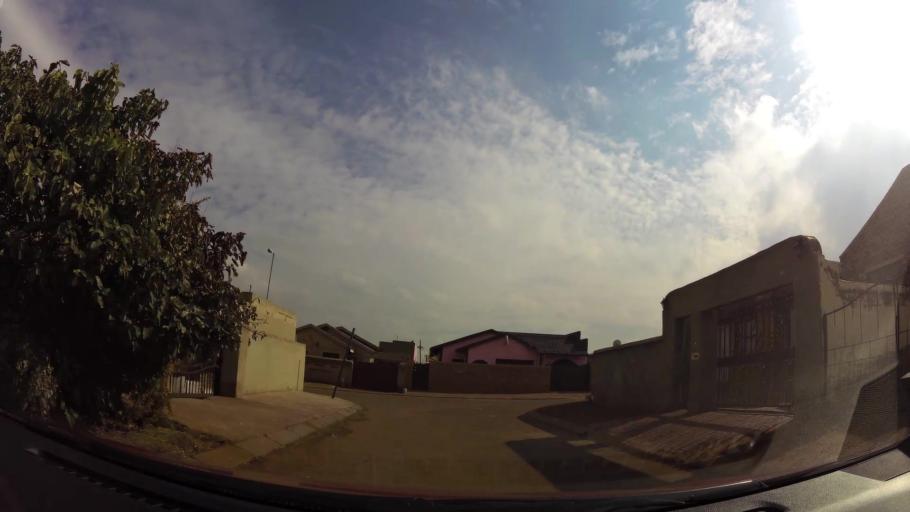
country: ZA
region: Gauteng
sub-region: City of Johannesburg Metropolitan Municipality
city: Soweto
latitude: -26.2573
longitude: 27.8164
